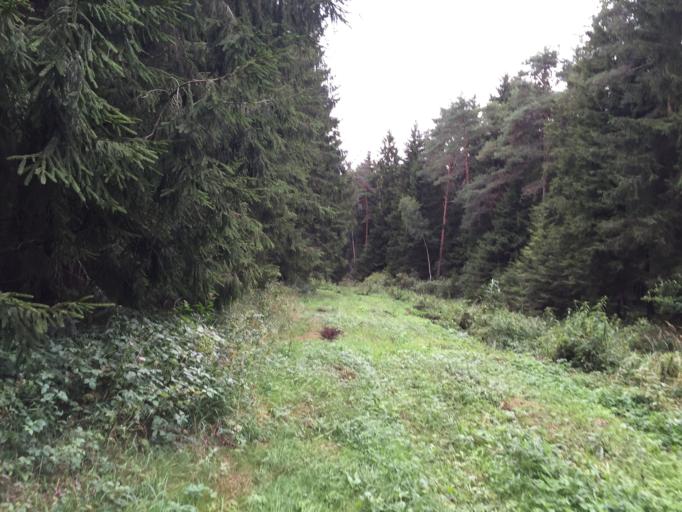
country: LV
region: Jaunpils
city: Jaunpils
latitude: 56.7293
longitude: 23.0881
